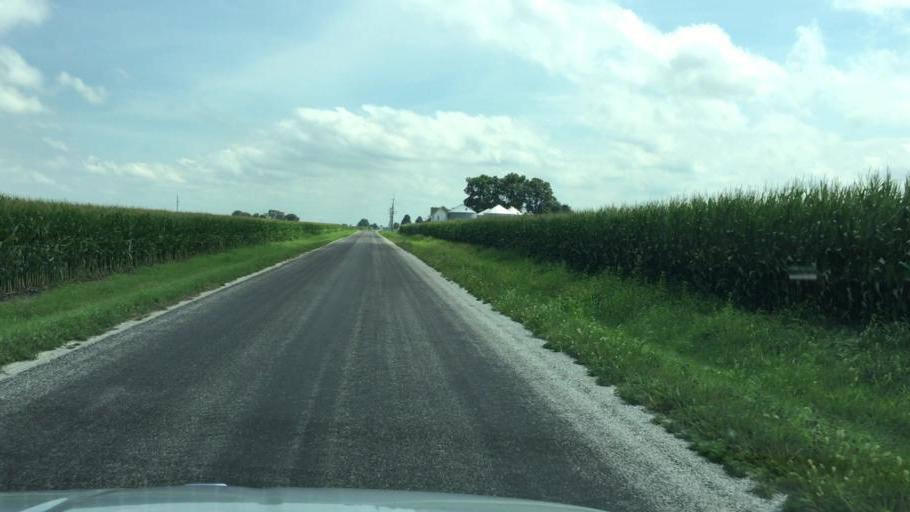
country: US
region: Illinois
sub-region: Hancock County
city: Carthage
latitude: 40.5243
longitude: -91.1771
